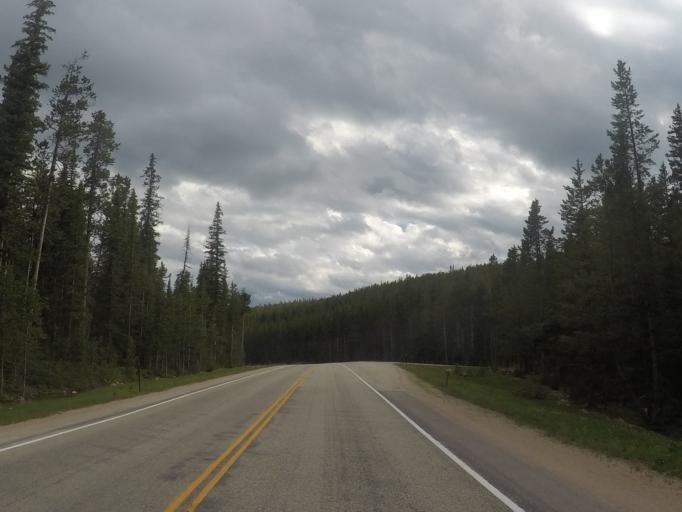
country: US
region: Wyoming
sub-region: Sheridan County
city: Sheridan
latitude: 44.7768
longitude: -107.4384
